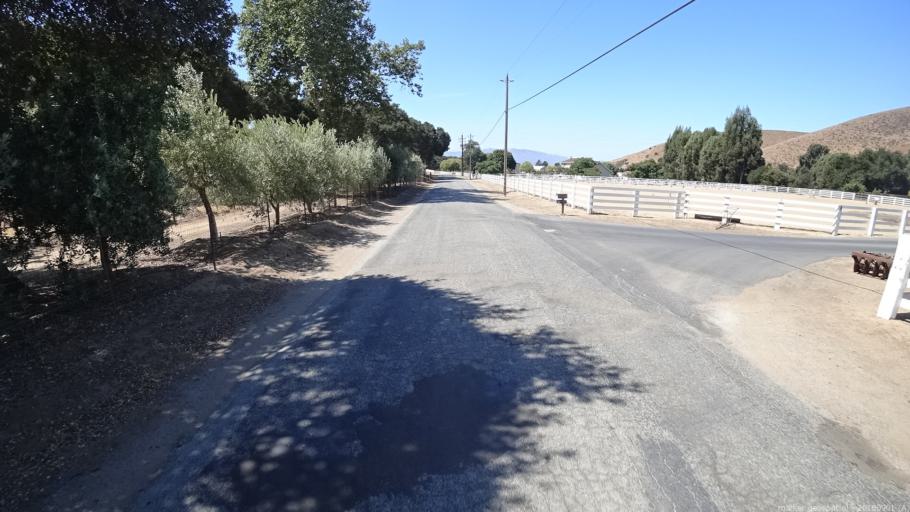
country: US
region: California
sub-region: Monterey County
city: Chualar
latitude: 36.6002
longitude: -121.4334
